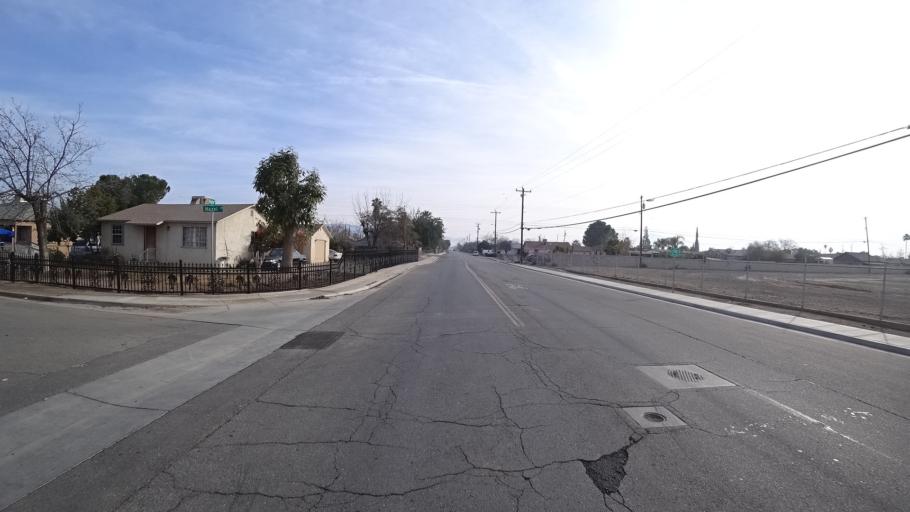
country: US
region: California
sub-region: Kern County
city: Bakersfield
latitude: 35.3614
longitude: -118.9635
